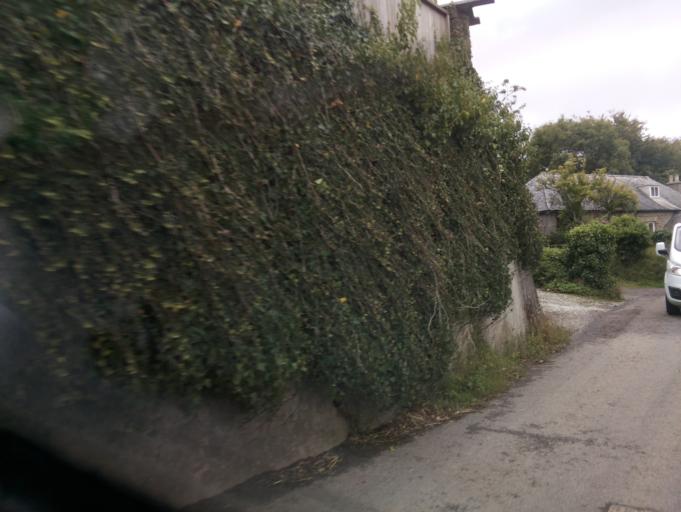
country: GB
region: England
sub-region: Devon
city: Kingsbridge
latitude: 50.2707
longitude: -3.8262
